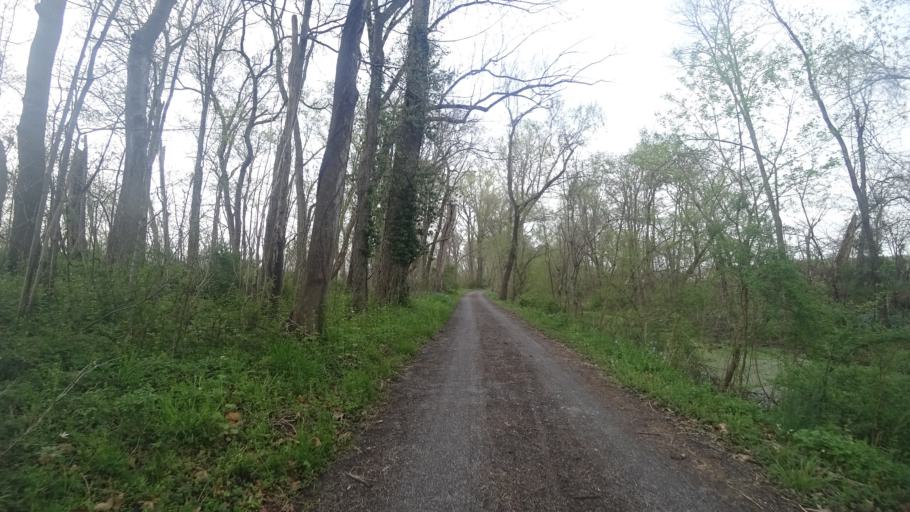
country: US
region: Virginia
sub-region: Loudoun County
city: Leesburg
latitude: 39.1283
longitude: -77.5150
